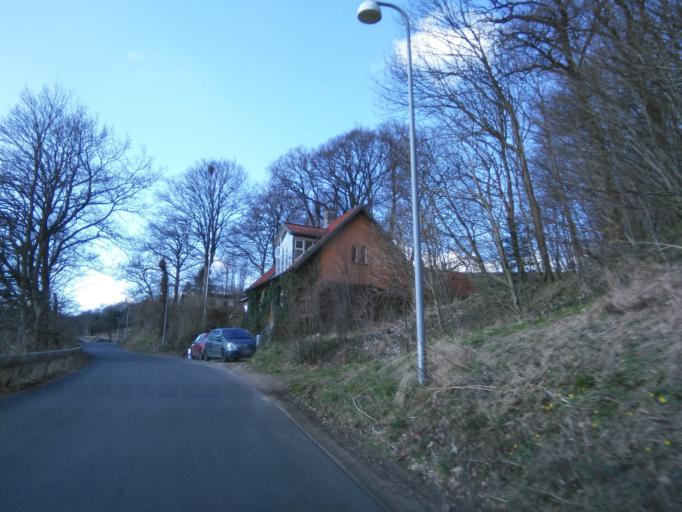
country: DK
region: Central Jutland
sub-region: Skanderborg Kommune
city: Ry
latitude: 56.1269
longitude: 9.7246
